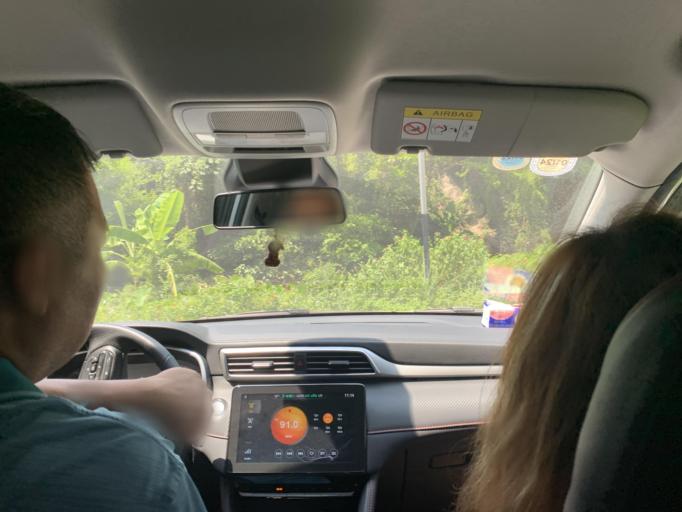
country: VN
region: Ninh Binh
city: Thanh Pho Ninh Binh
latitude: 20.2237
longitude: 105.9314
